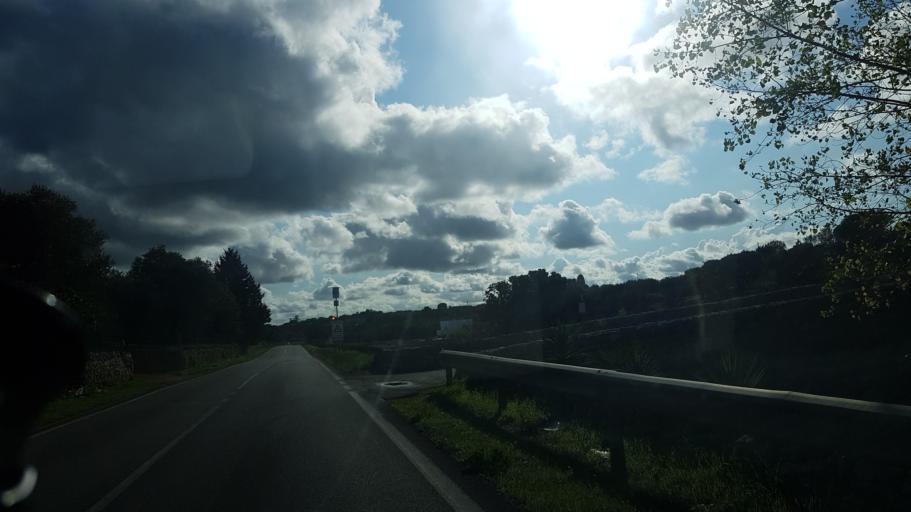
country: IT
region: Apulia
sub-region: Provincia di Brindisi
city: Ostuni
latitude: 40.6899
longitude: 17.5890
